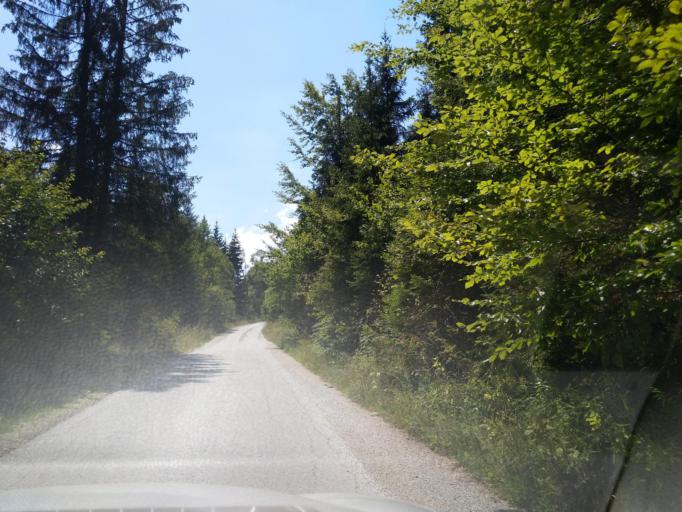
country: RS
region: Central Serbia
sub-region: Zlatiborski Okrug
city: Nova Varos
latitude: 43.4727
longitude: 19.9634
